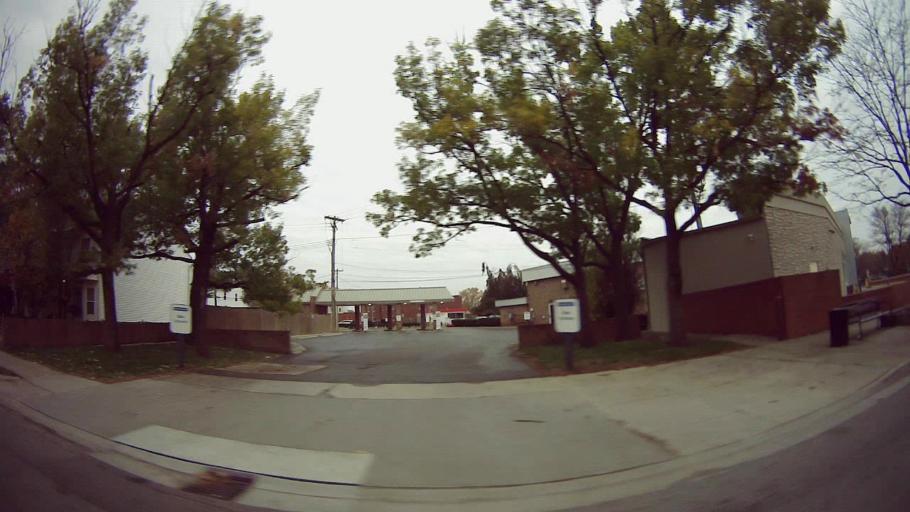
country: US
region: Michigan
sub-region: Oakland County
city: Birmingham
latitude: 42.5320
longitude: -83.2012
